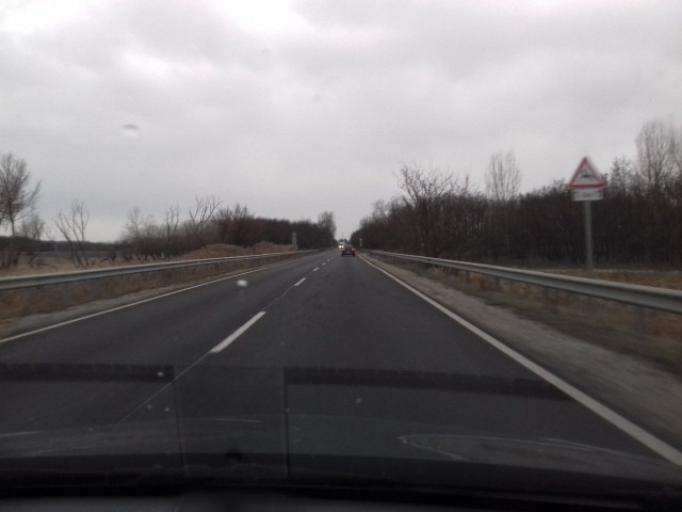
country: HU
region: Szabolcs-Szatmar-Bereg
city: Nyirbogdany
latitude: 48.0341
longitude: 21.8558
